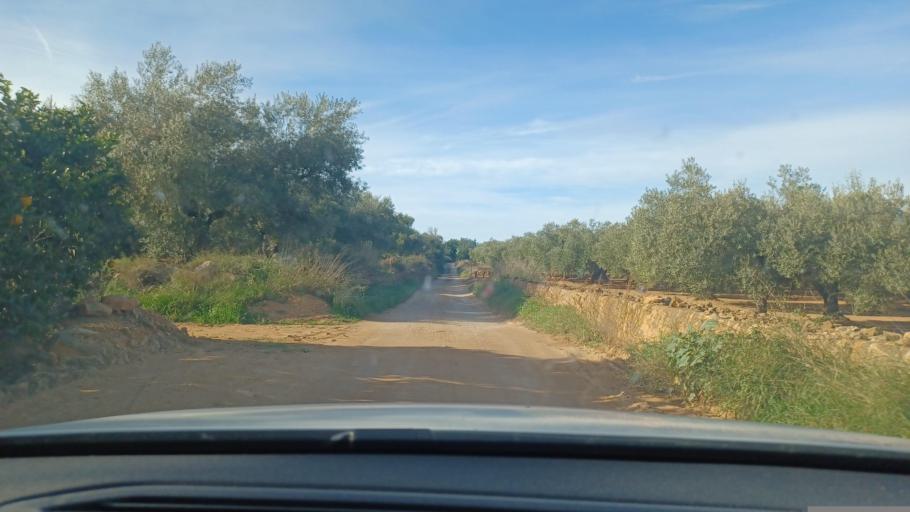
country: ES
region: Catalonia
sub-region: Provincia de Tarragona
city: Santa Barbara
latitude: 40.6842
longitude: 0.4983
